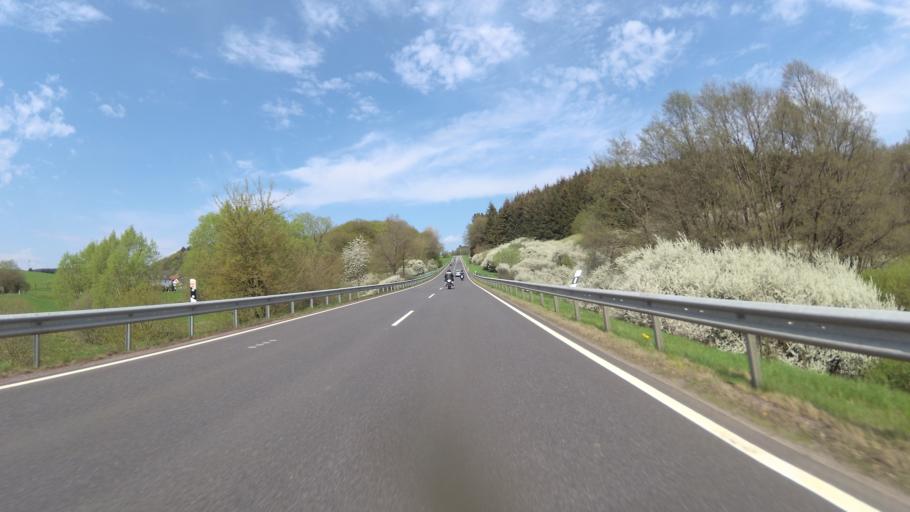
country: DE
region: Rheinland-Pfalz
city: Horschhausen
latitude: 50.2454
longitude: 6.9299
